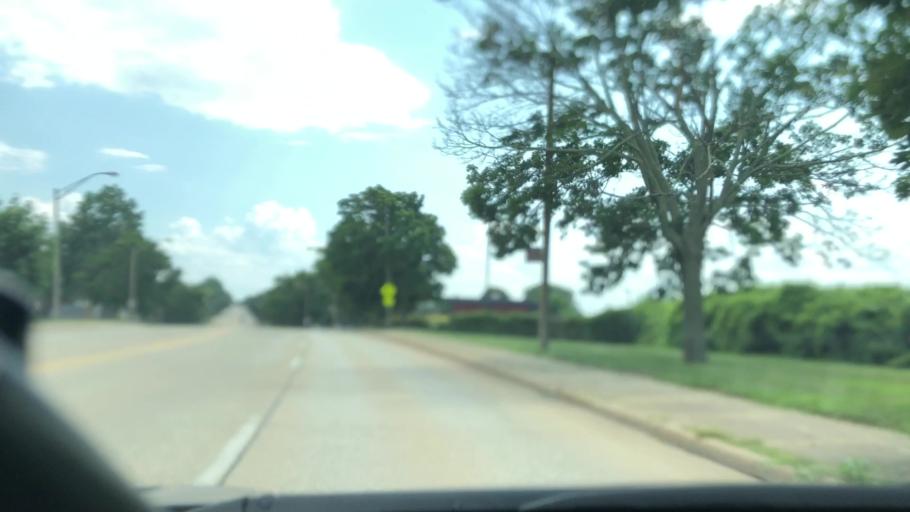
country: US
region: Ohio
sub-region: Summit County
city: Akron
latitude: 41.0715
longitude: -81.5205
